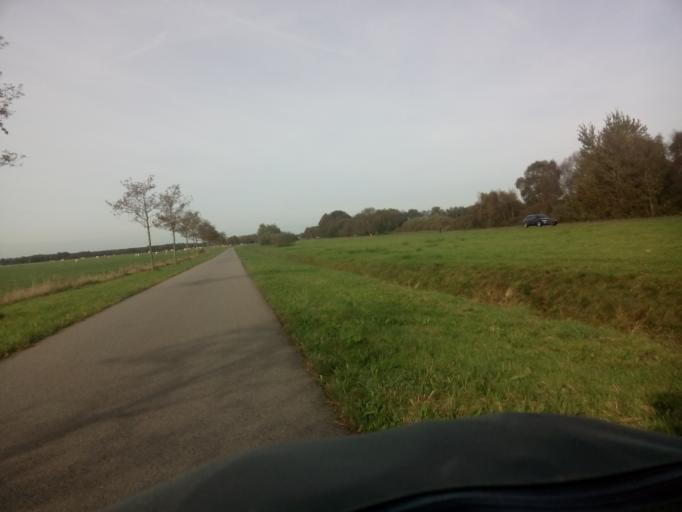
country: NL
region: Drenthe
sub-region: Gemeente Hoogeveen
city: Hoogeveen
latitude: 52.7518
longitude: 6.4566
